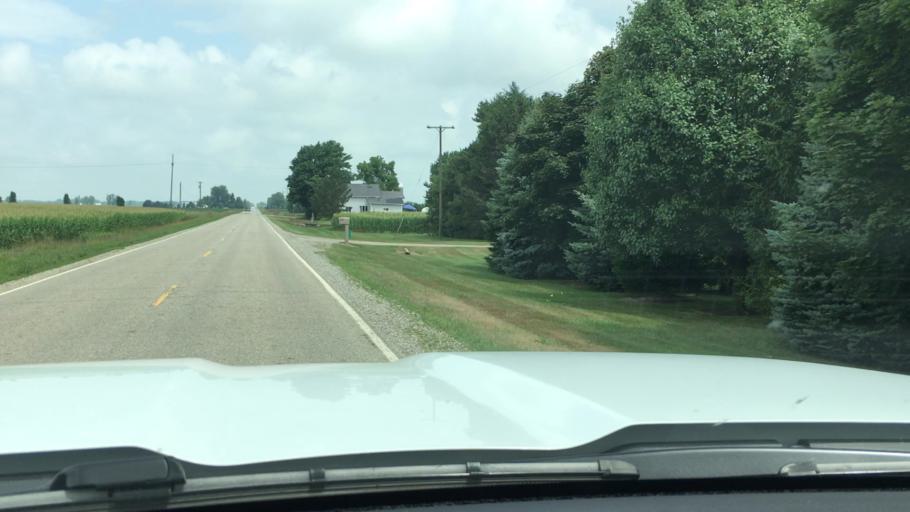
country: US
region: Michigan
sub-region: Sanilac County
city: Marlette
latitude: 43.3855
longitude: -83.0069
